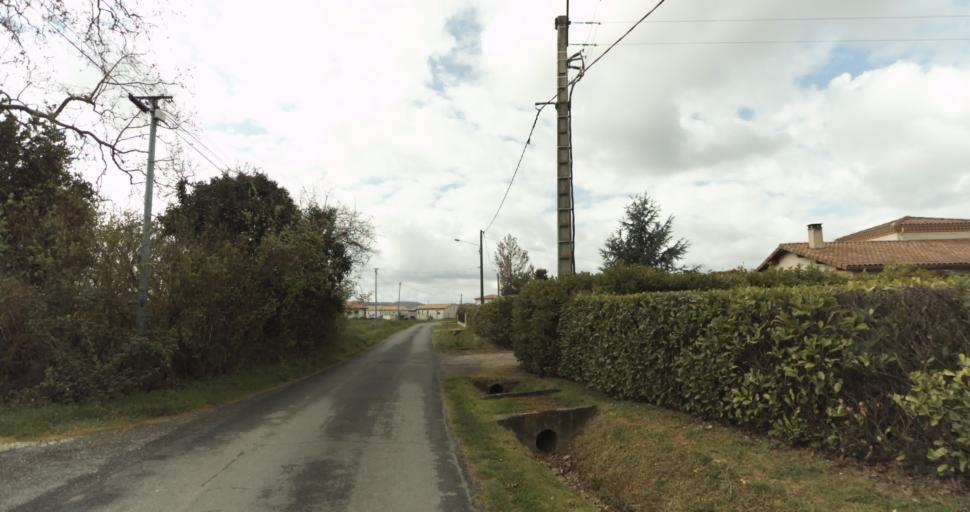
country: FR
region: Midi-Pyrenees
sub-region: Departement de la Haute-Garonne
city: Auterive
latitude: 43.3442
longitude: 1.4587
